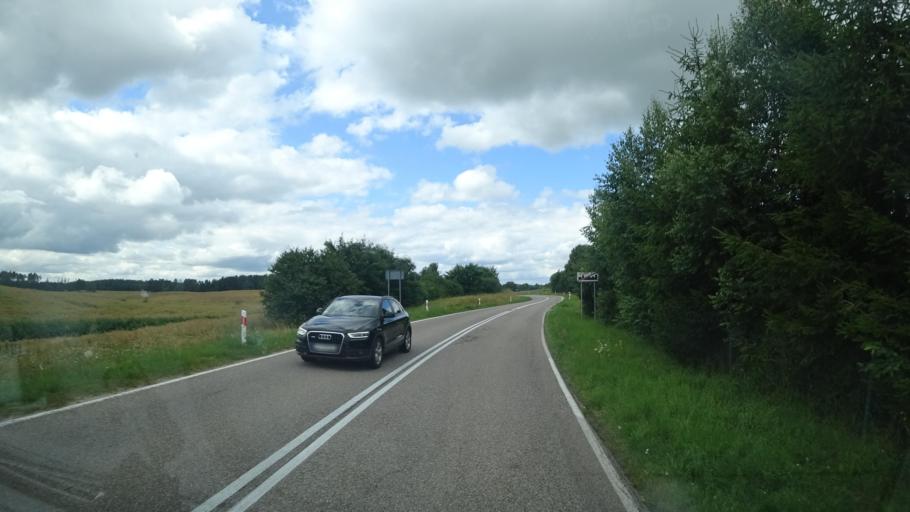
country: PL
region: Warmian-Masurian Voivodeship
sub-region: Powiat goldapski
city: Banie Mazurskie
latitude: 54.2088
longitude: 22.1847
